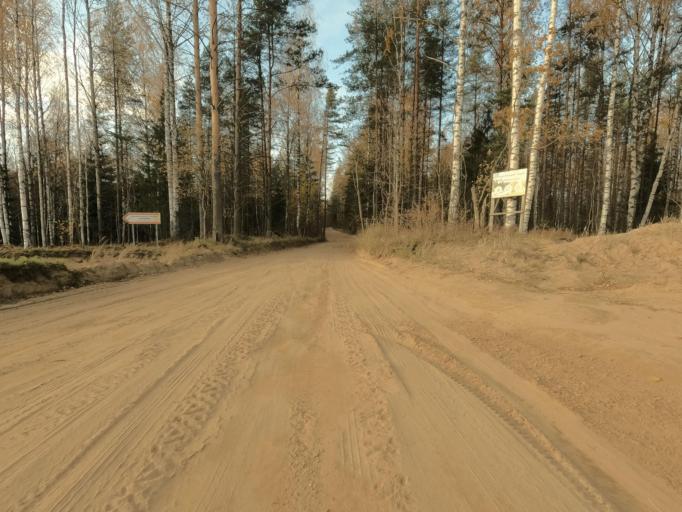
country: RU
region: Leningrad
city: Priladozhskiy
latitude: 59.7394
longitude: 31.3162
